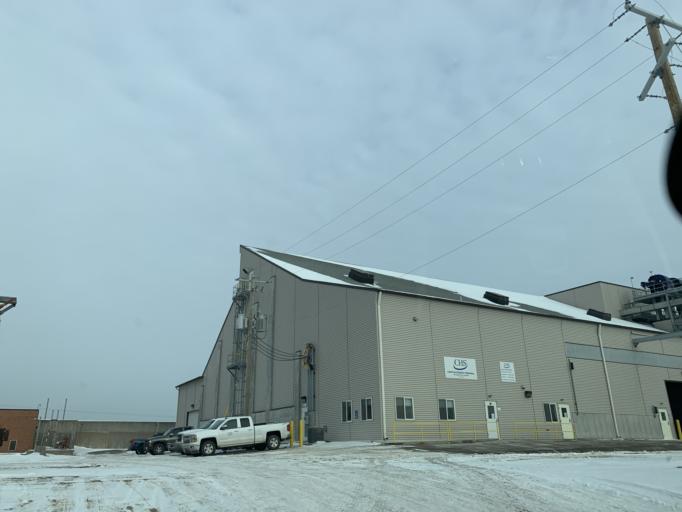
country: US
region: Minnesota
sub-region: Ramsey County
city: Saint Paul
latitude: 44.9452
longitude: -93.0769
